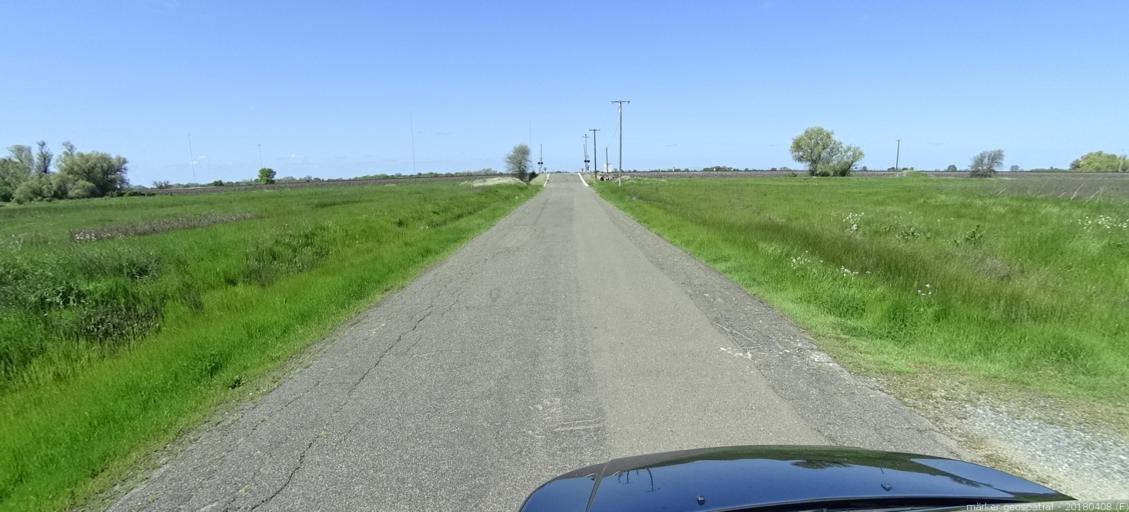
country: US
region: California
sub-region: San Joaquin County
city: Thornton
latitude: 38.2759
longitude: -121.4373
